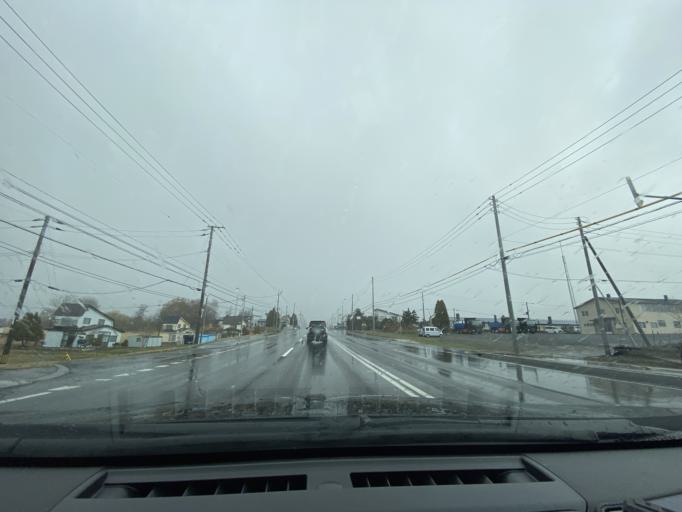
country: JP
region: Hokkaido
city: Takikawa
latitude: 43.6173
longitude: 141.9372
